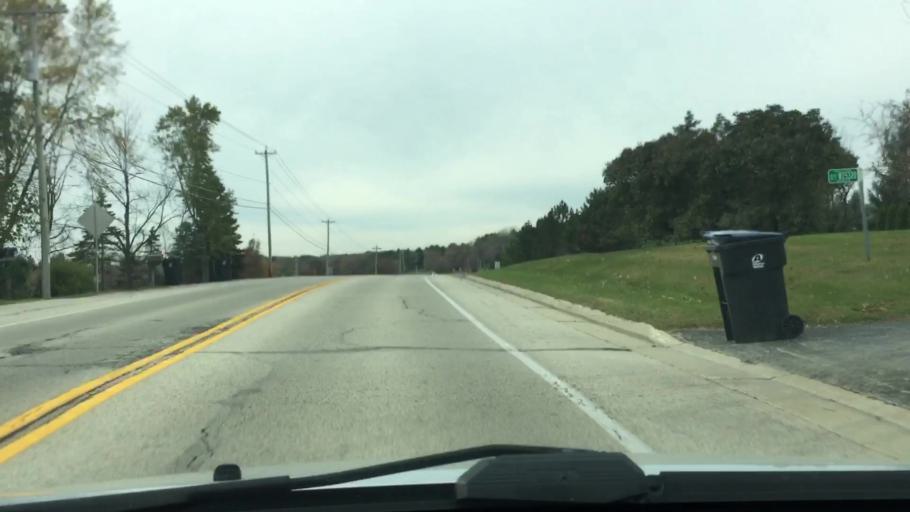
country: US
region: Wisconsin
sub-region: Waukesha County
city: Big Bend
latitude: 42.9034
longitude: -88.2547
